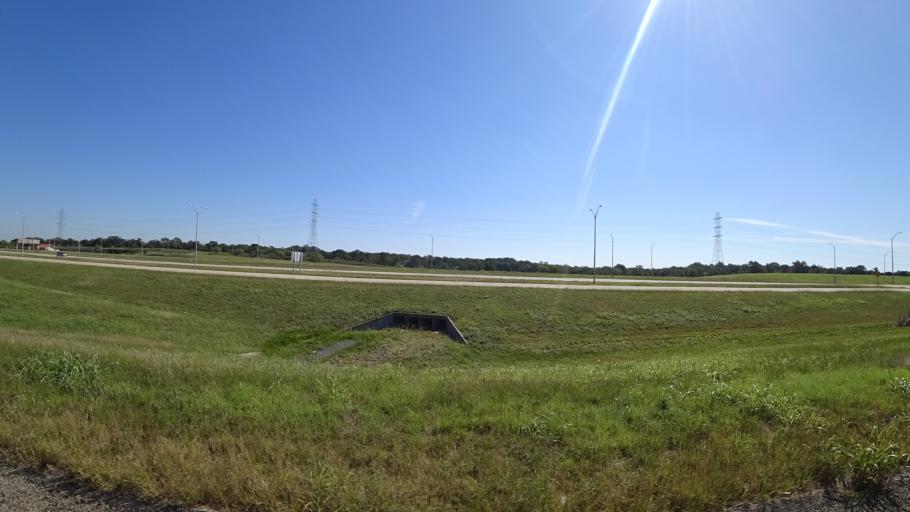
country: US
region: Texas
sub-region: Travis County
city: Hornsby Bend
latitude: 30.2670
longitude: -97.5972
